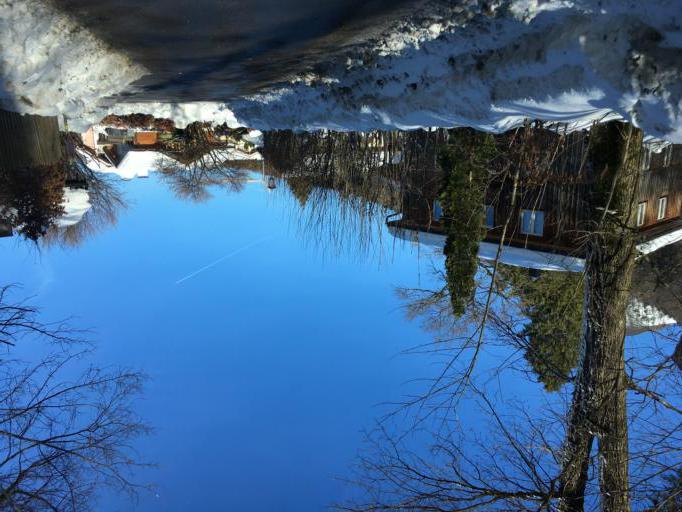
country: DE
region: Bavaria
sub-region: Upper Bavaria
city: Aschau im Chiemgau
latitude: 47.7659
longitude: 12.3156
